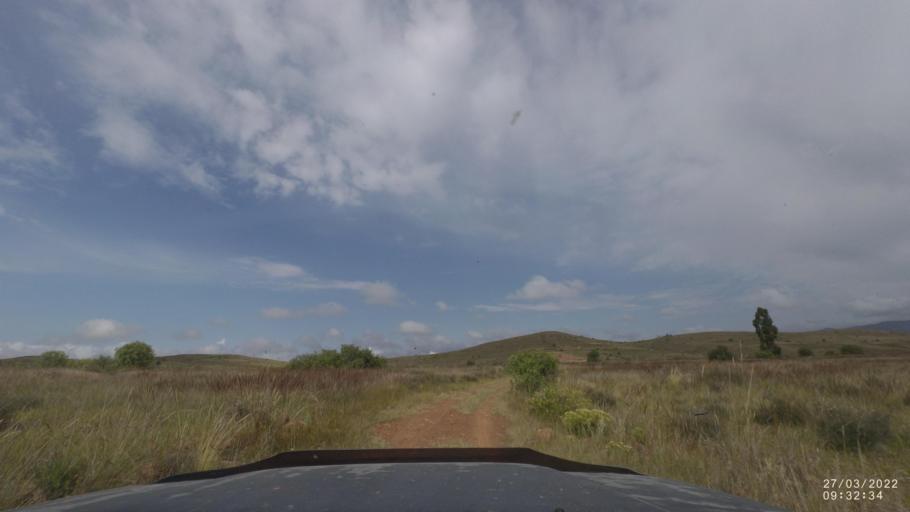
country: BO
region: Cochabamba
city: Cliza
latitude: -17.7377
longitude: -65.8853
